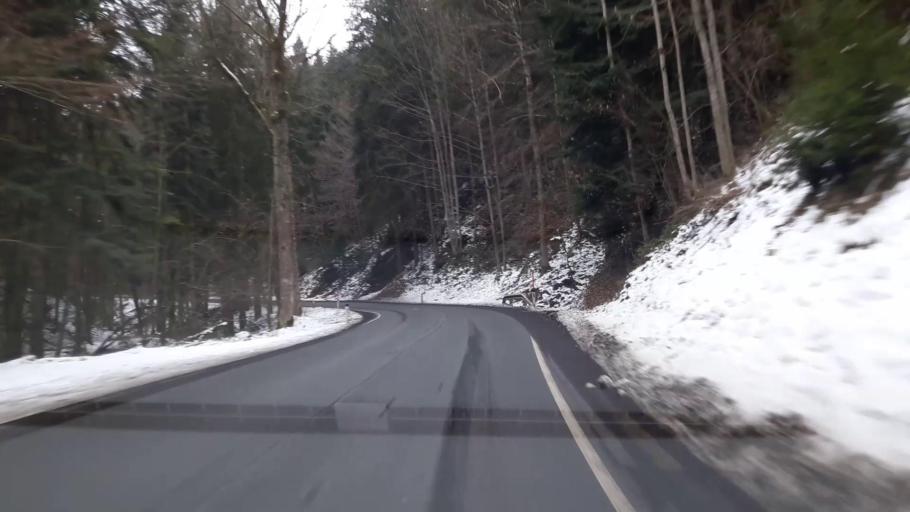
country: AT
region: Lower Austria
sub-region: Politischer Bezirk Neunkirchen
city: Feistritz am Wechsel
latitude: 47.5548
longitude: 16.0781
